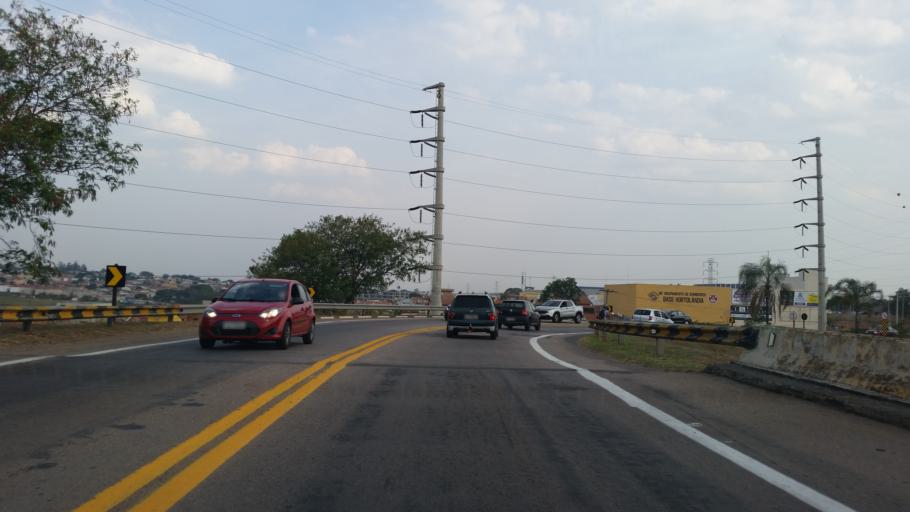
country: BR
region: Sao Paulo
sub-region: Hortolandia
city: Hortolandia
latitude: -22.8961
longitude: -47.1870
